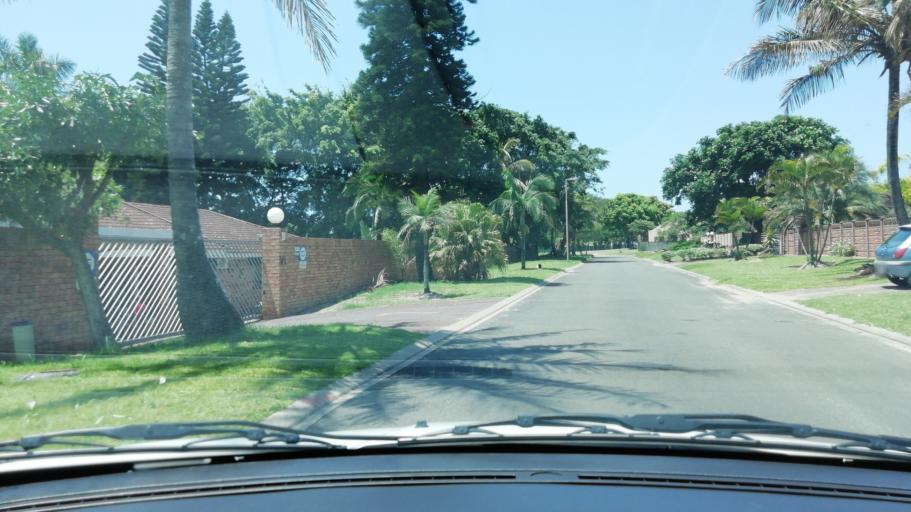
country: ZA
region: KwaZulu-Natal
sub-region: uThungulu District Municipality
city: Richards Bay
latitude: -28.7346
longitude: 32.0462
